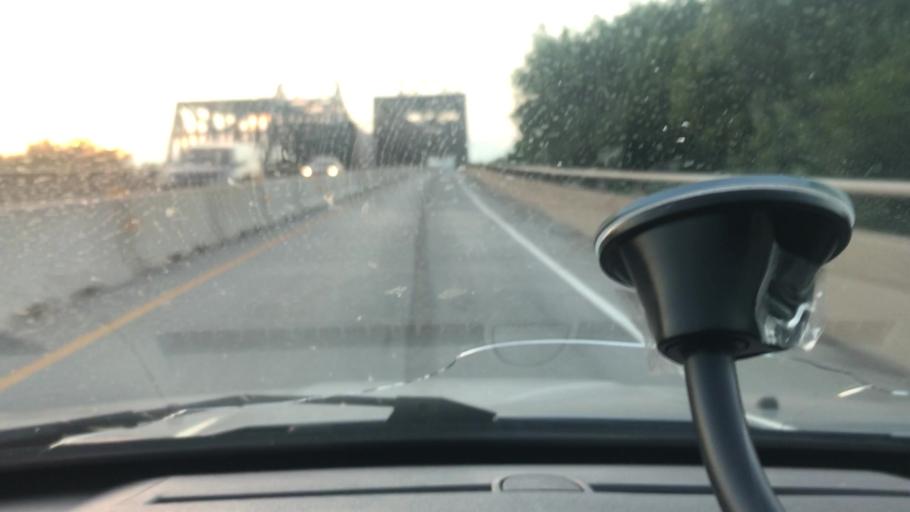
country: US
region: Illinois
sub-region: Tazewell County
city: North Pekin
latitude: 40.6332
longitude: -89.6200
